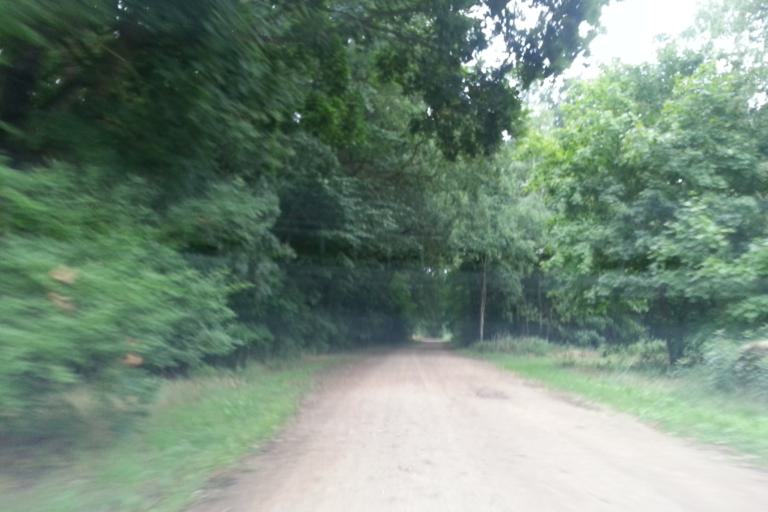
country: DE
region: Mecklenburg-Vorpommern
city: Ferdinandshof
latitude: 53.6560
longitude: 13.9351
